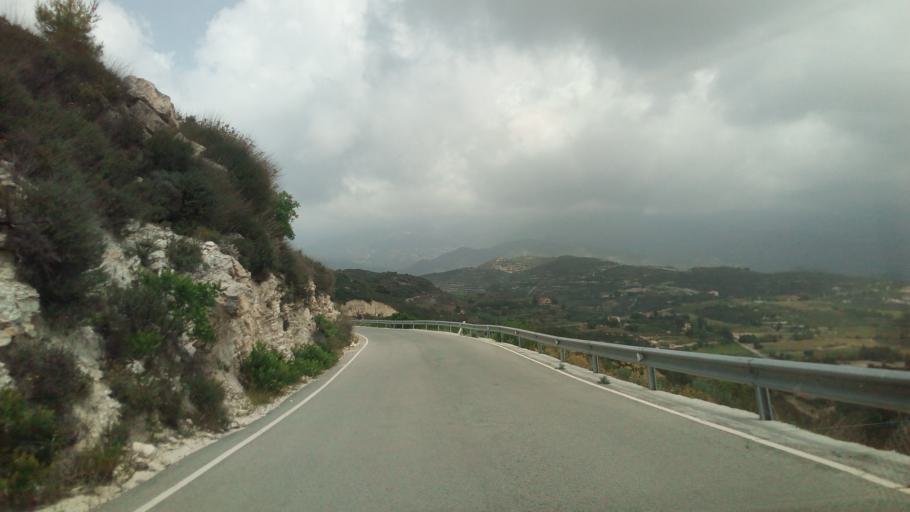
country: CY
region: Limassol
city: Pachna
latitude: 34.8364
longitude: 32.8782
